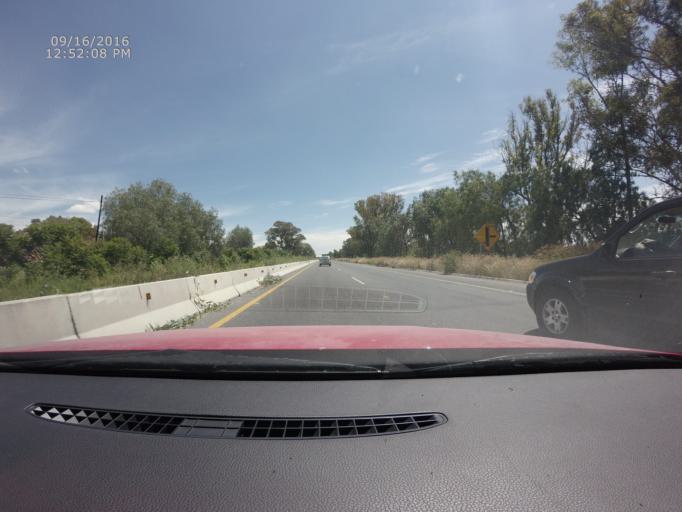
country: MX
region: Queretaro
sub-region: Colon
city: Purisima de Cubos (La Purisima)
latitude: 20.6162
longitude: -100.1469
